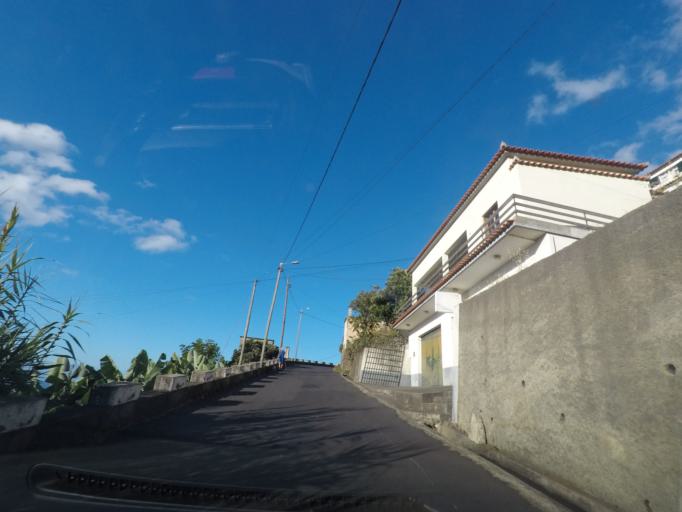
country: PT
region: Madeira
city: Ponta do Sol
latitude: 32.6908
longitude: -17.0860
